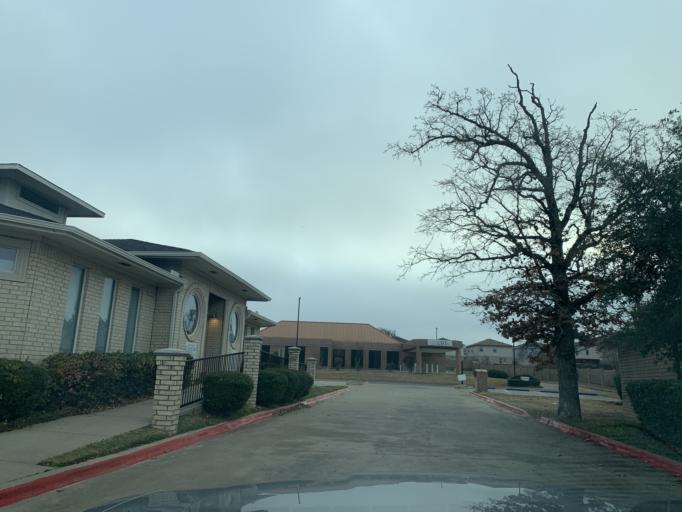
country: US
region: Texas
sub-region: Tarrant County
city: Bedford
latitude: 32.8350
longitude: -97.1426
